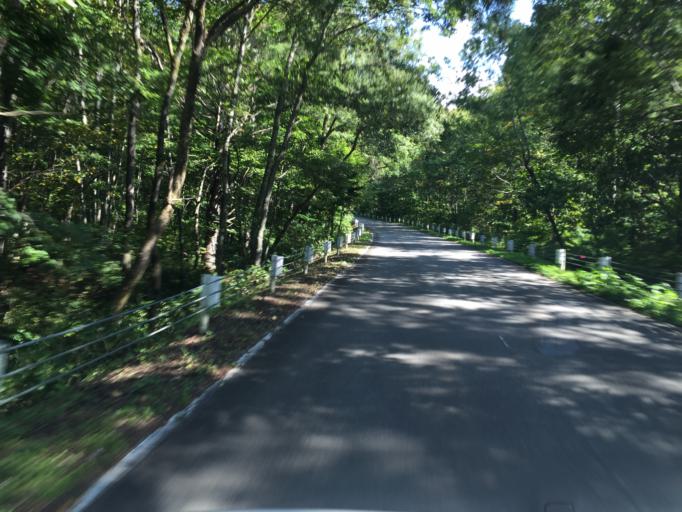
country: JP
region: Fukushima
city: Inawashiro
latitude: 37.6515
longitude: 140.1997
